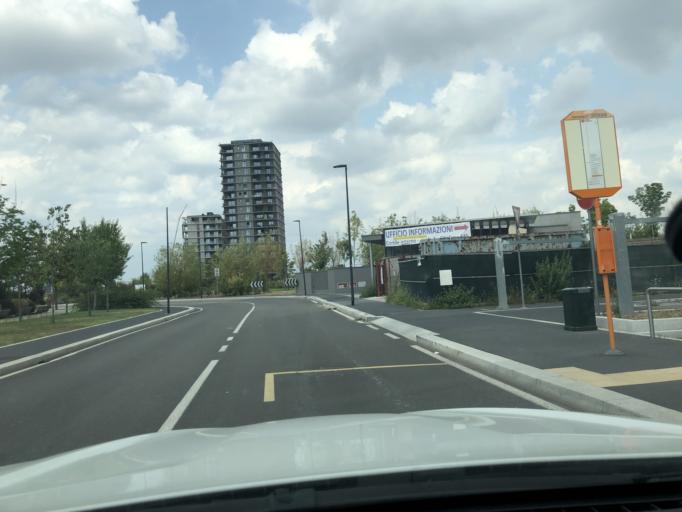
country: IT
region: Lombardy
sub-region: Citta metropolitana di Milano
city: Pero
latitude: 45.5062
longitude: 9.1039
